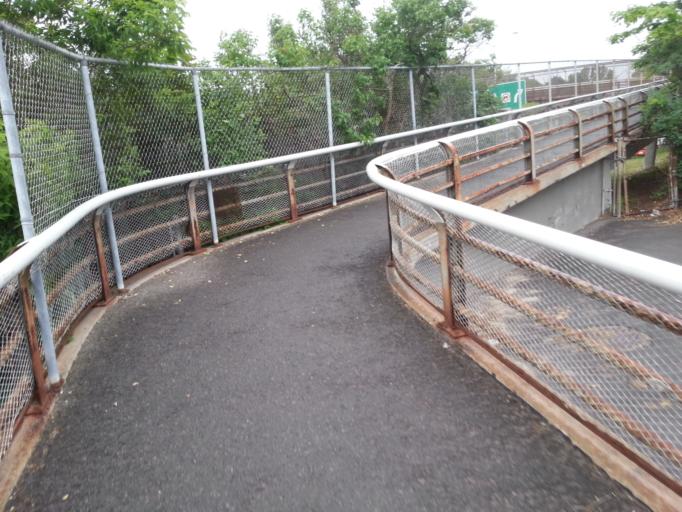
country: CA
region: Ontario
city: Ottawa
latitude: 45.3943
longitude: -75.7310
